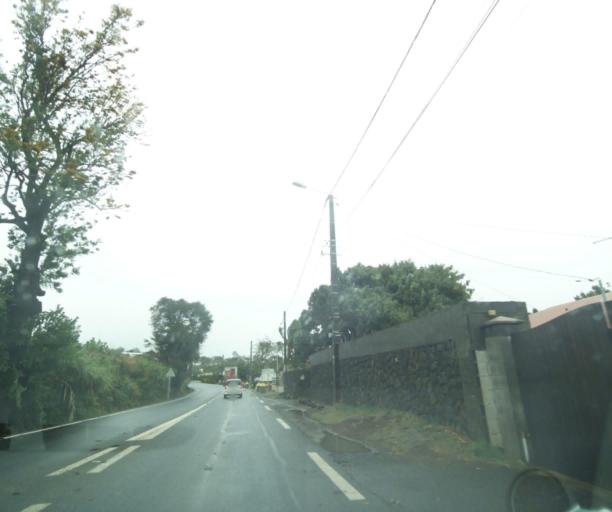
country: RE
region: Reunion
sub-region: Reunion
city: Saint-Paul
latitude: -21.0411
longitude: 55.2680
